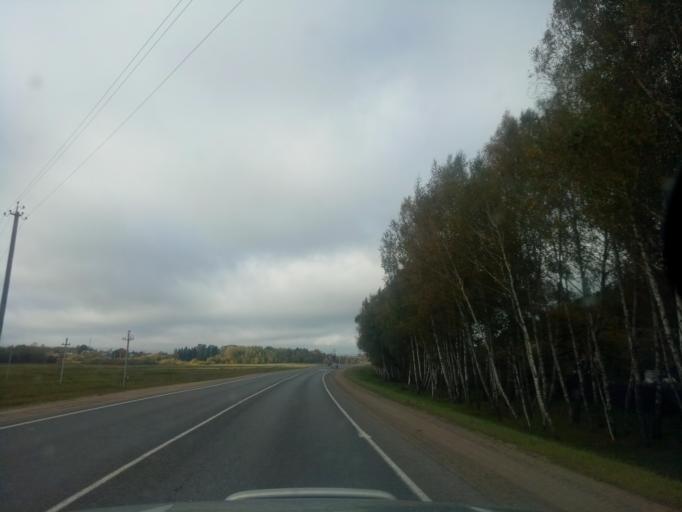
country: BY
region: Minsk
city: Zaslawye
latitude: 53.9937
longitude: 27.2949
